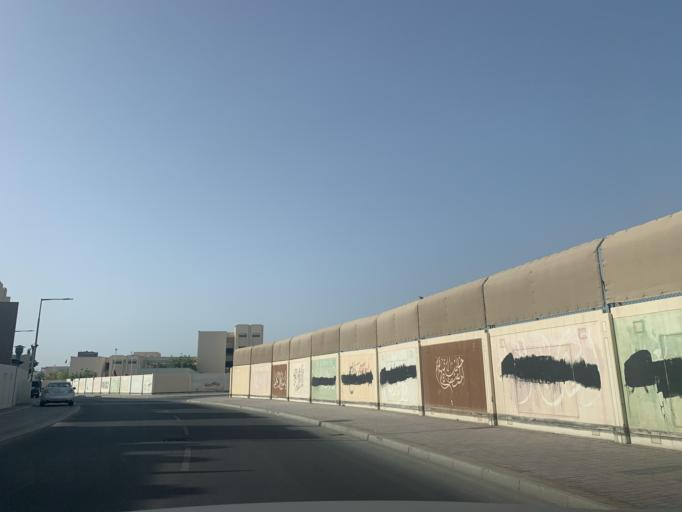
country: BH
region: Northern
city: Sitrah
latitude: 26.1630
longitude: 50.6289
